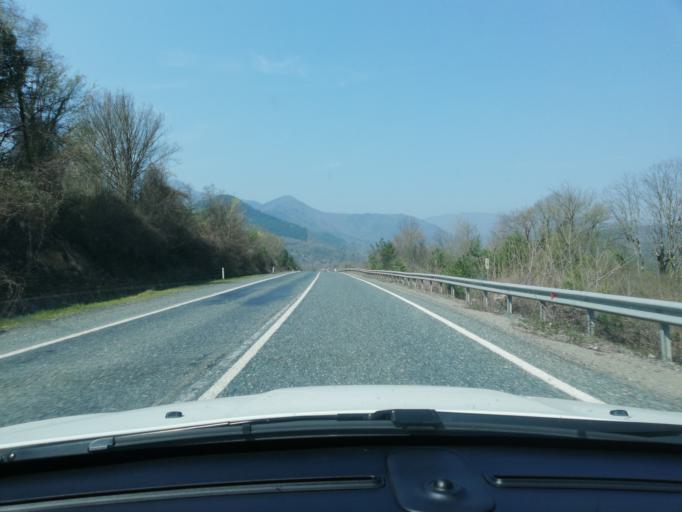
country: TR
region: Zonguldak
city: Gokcebey
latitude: 41.2290
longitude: 32.2022
